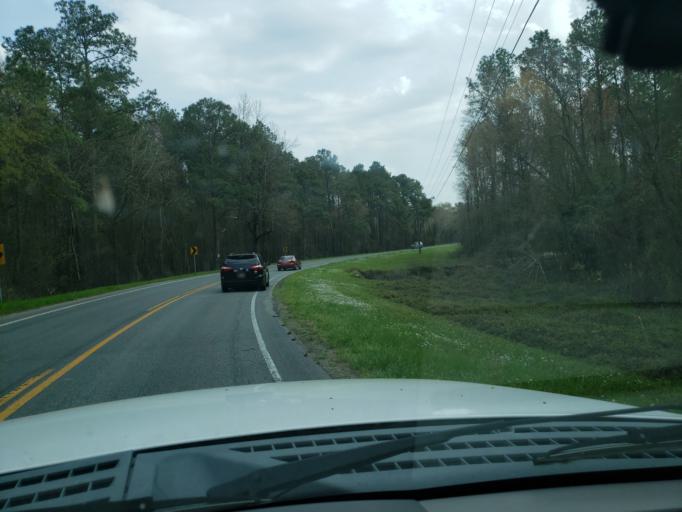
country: US
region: North Carolina
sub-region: Duplin County
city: Beulaville
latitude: 34.7884
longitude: -77.8394
